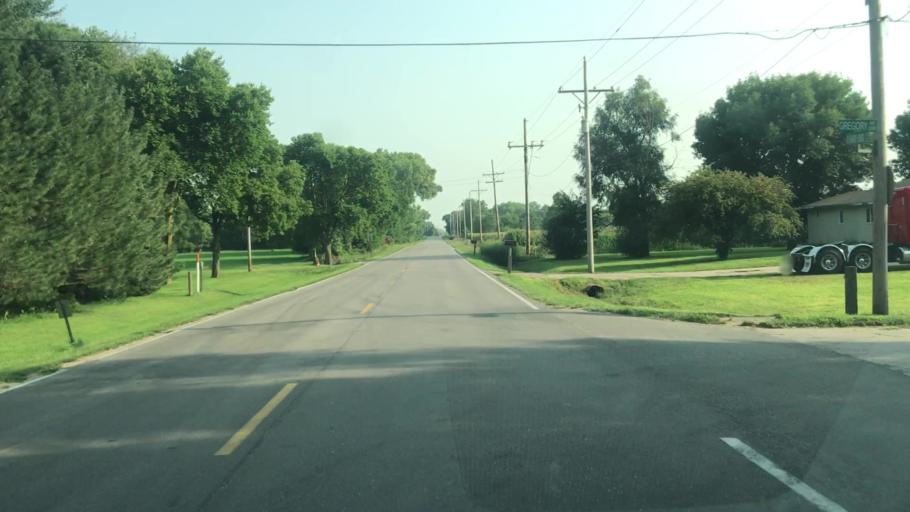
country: US
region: Nebraska
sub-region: Hall County
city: Grand Island
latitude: 40.9284
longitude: -98.3015
